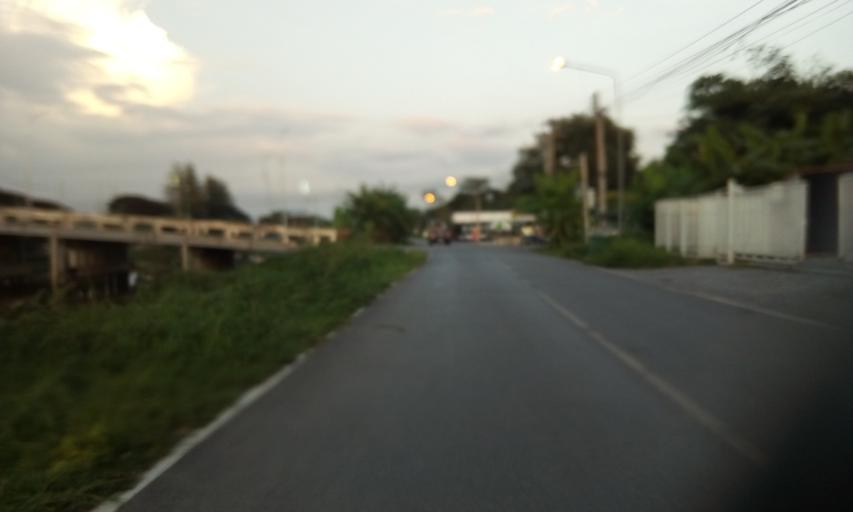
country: TH
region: Pathum Thani
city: Ban Rangsit
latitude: 14.0418
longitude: 100.7946
